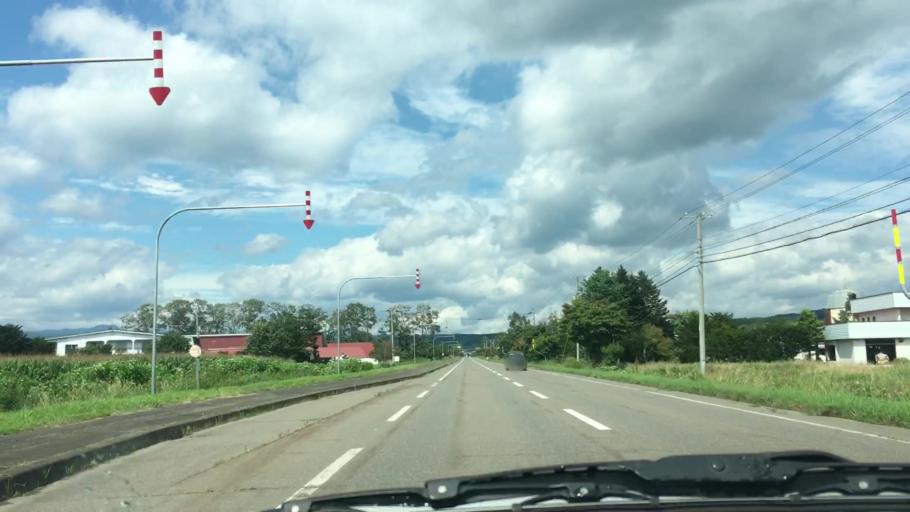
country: JP
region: Hokkaido
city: Otofuke
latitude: 43.2846
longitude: 143.3068
